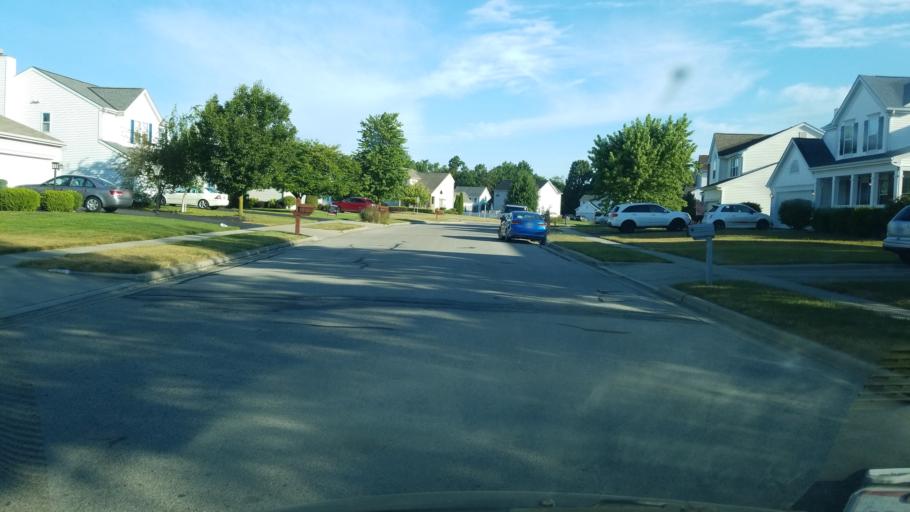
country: US
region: Ohio
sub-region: Delaware County
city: Lewis Center
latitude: 40.1685
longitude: -82.9978
